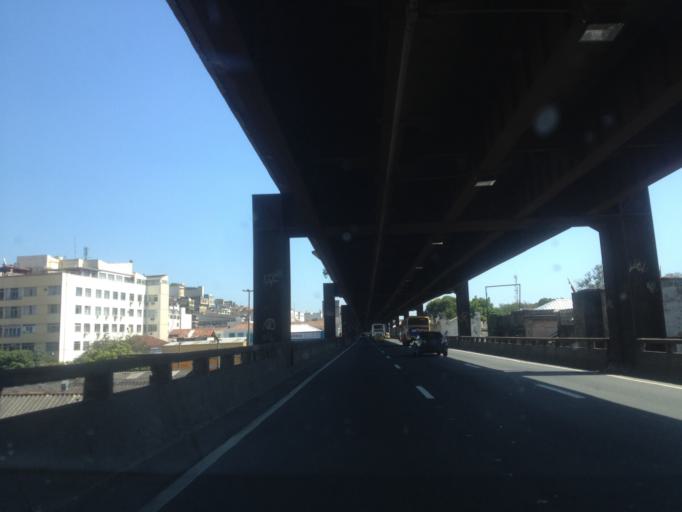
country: BR
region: Rio de Janeiro
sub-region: Rio De Janeiro
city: Rio de Janeiro
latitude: -22.9044
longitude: -43.2149
